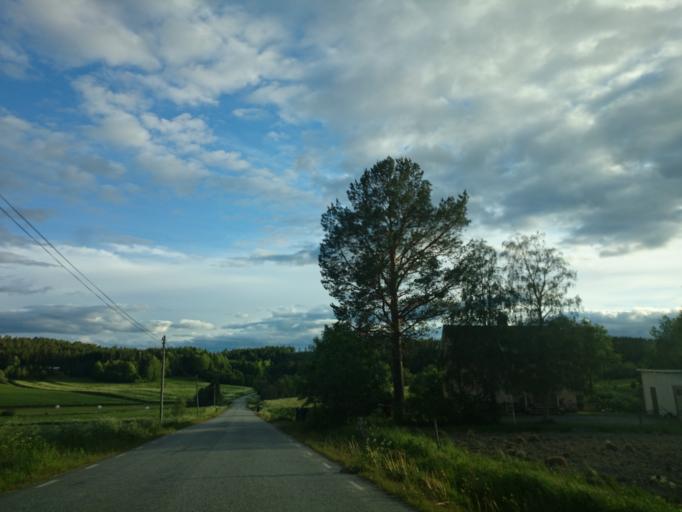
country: SE
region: Vaesternorrland
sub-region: Haernoesands Kommun
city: Haernoesand
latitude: 62.5599
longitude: 17.8347
